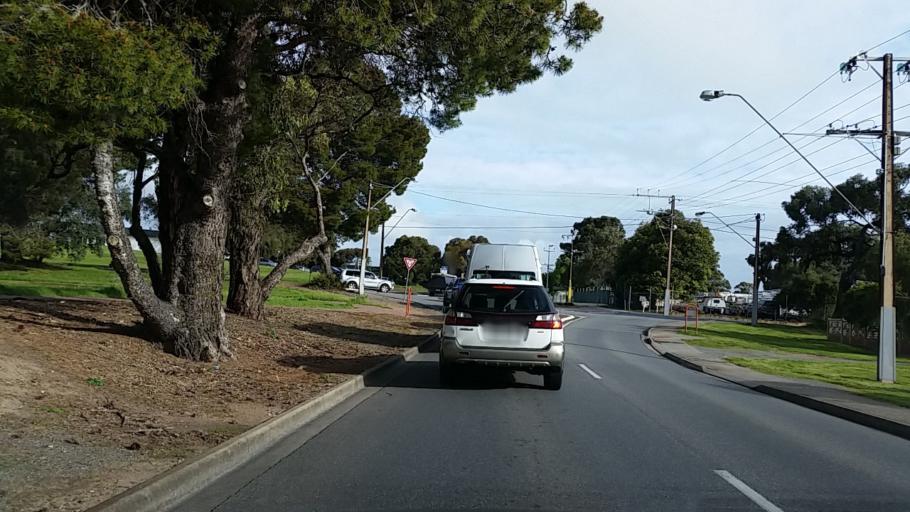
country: AU
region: South Australia
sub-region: Onkaparinga
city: Reynella
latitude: -35.1042
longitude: 138.5348
